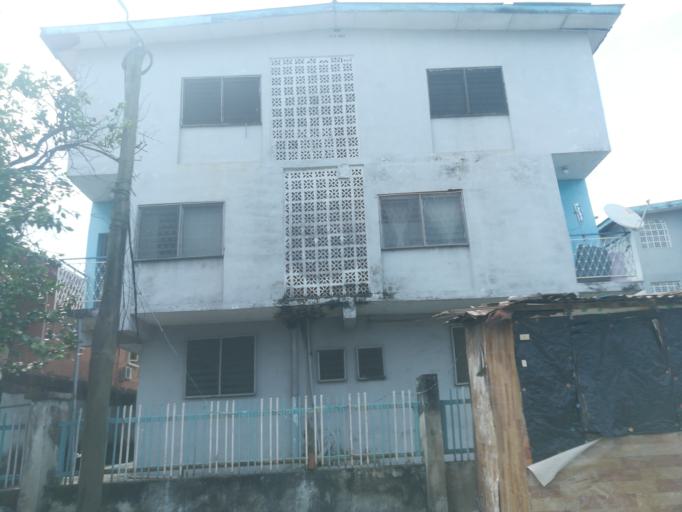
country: NG
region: Lagos
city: Somolu
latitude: 6.5279
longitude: 3.3822
